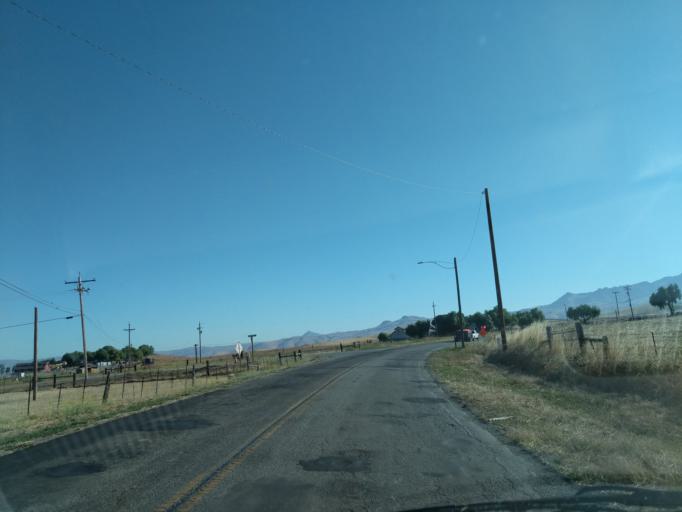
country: US
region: California
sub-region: San Benito County
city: Ridgemark
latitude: 36.8251
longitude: -121.3454
